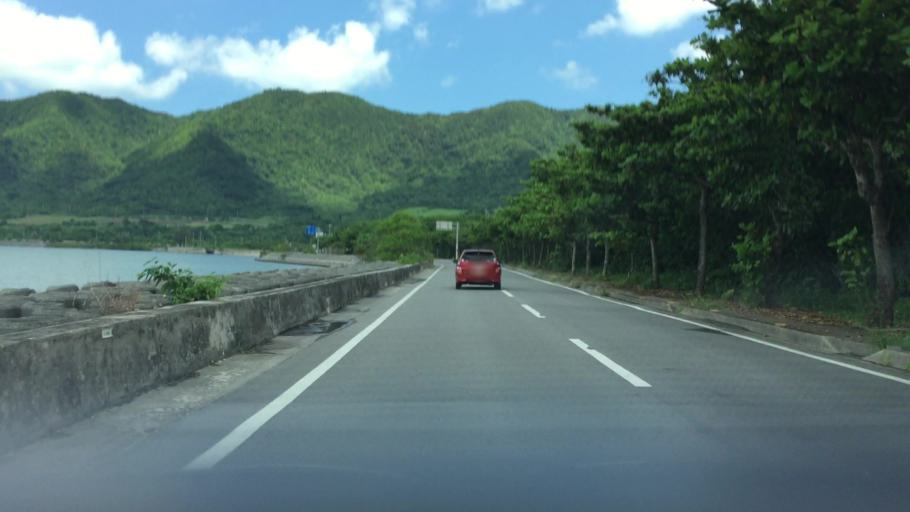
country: JP
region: Okinawa
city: Ishigaki
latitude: 24.4069
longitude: 124.1439
